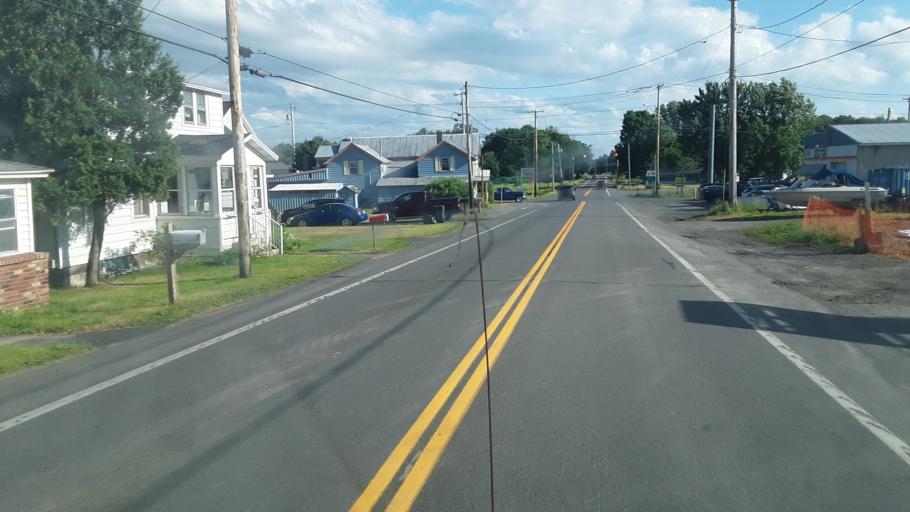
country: US
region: New York
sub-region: Oneida County
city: Rome
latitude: 43.3044
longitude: -75.4731
